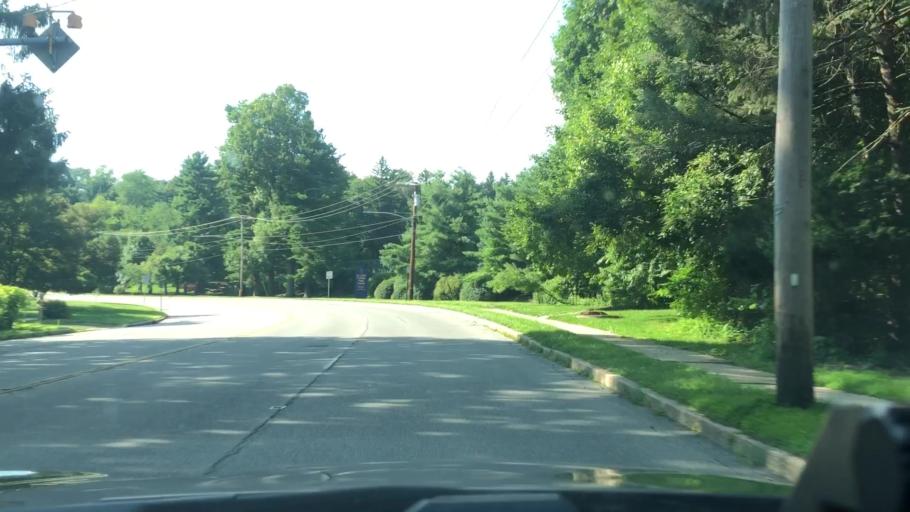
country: US
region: Pennsylvania
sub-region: Montgomery County
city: Wyndmoor
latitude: 40.0918
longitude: -75.1876
